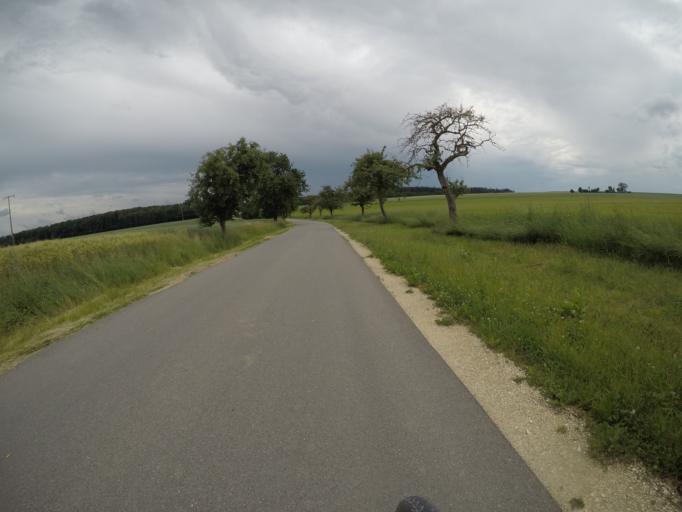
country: DE
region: Baden-Wuerttemberg
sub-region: Tuebingen Region
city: Dornstadt
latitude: 48.4885
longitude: 9.9523
